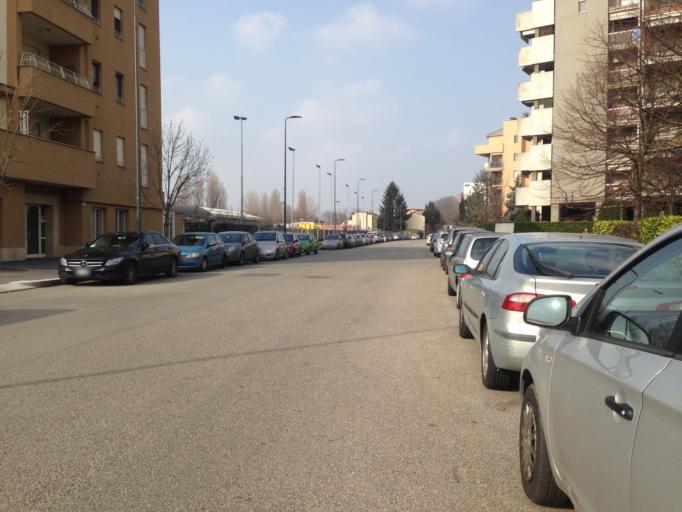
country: IT
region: Lombardy
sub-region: Citta metropolitana di Milano
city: Cesano Boscone
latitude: 45.4714
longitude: 9.1053
